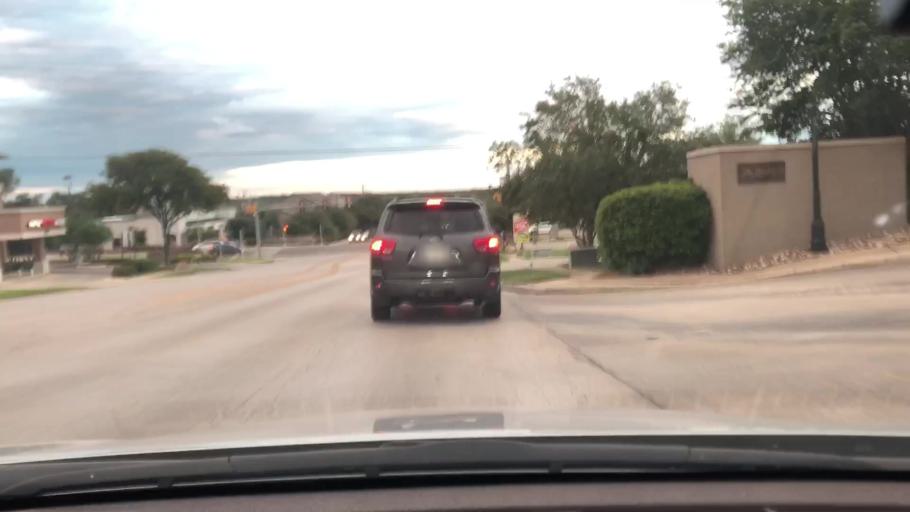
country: US
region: Texas
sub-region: Bexar County
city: Shavano Park
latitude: 29.5938
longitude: -98.5292
